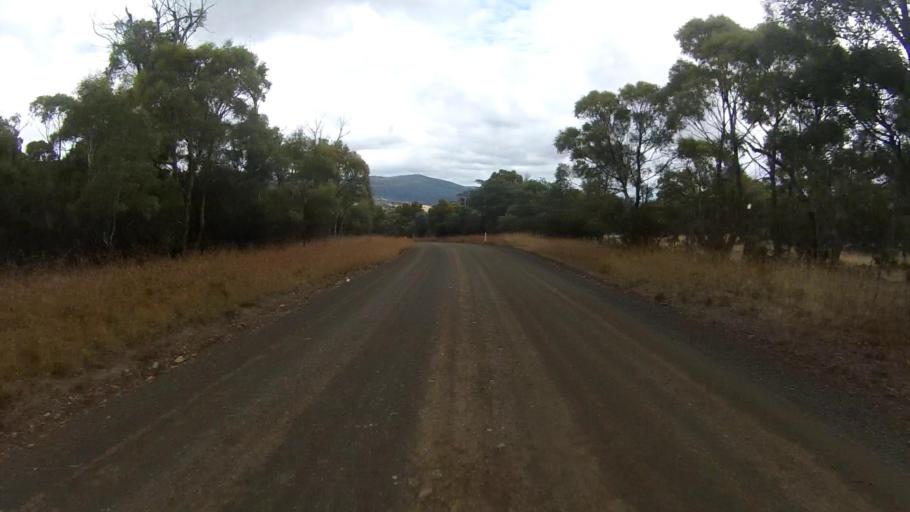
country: AU
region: Tasmania
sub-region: Break O'Day
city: St Helens
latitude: -41.8204
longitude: 147.9911
